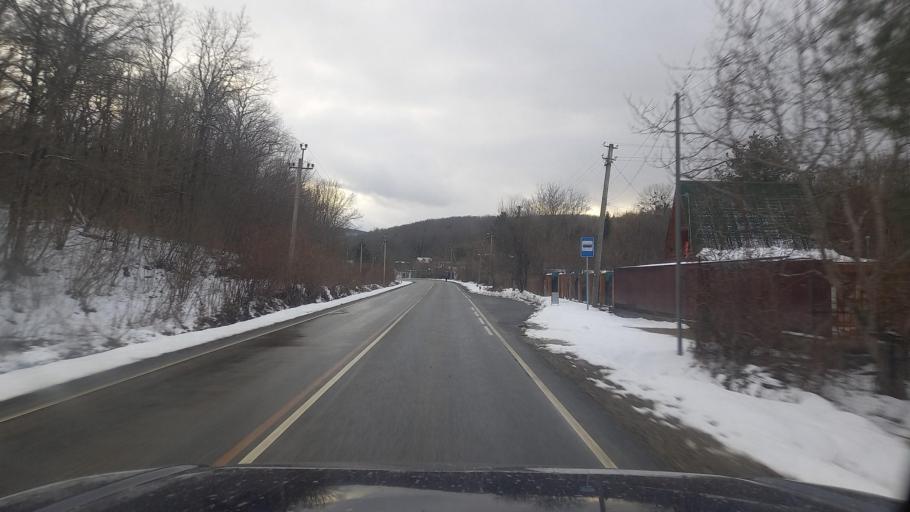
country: RU
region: Krasnodarskiy
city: Smolenskaya
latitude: 44.7065
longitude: 38.7332
